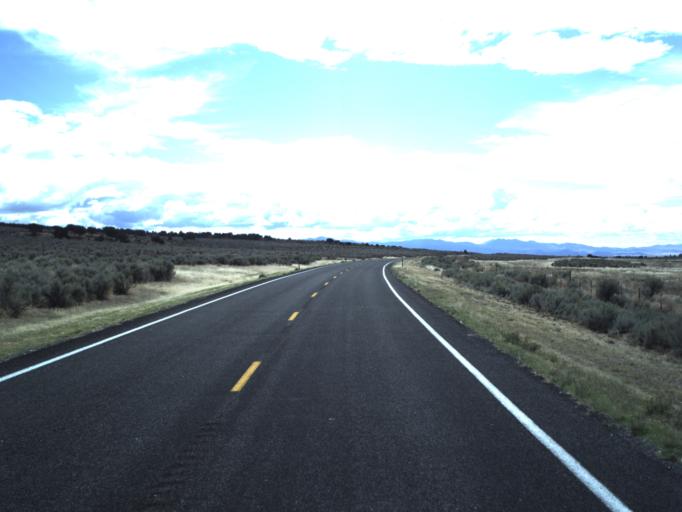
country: US
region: Utah
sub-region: Millard County
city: Fillmore
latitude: 39.0091
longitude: -112.4101
